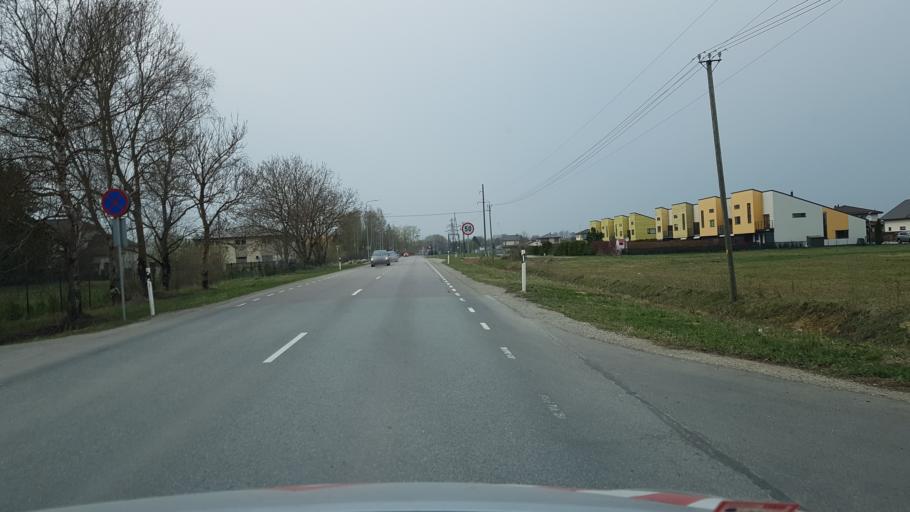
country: EE
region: Harju
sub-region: Joelaehtme vald
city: Loo
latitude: 59.4010
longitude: 24.9500
